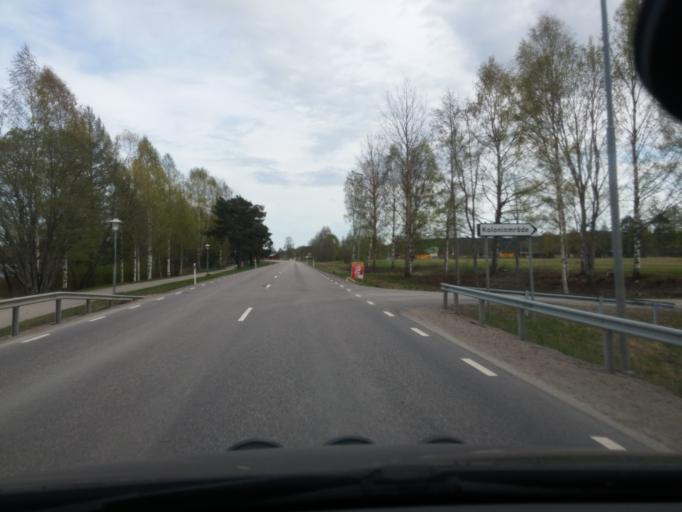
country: SE
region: Gaevleborg
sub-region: Ljusdals Kommun
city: Ljusdal
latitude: 61.8234
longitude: 16.0758
